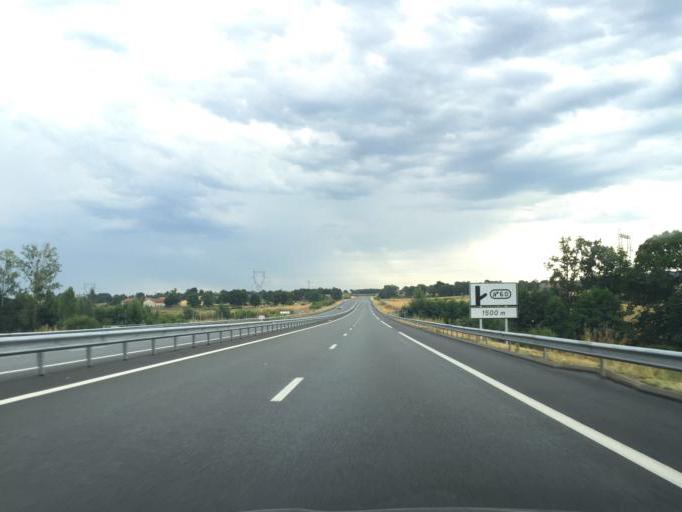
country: FR
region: Rhone-Alpes
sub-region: Departement de la Loire
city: La Pacaudiere
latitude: 46.1571
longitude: 3.8924
